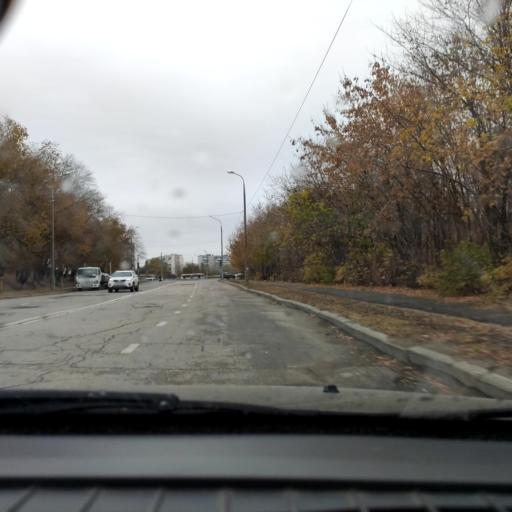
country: RU
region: Samara
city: Tol'yatti
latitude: 53.5044
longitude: 49.2534
